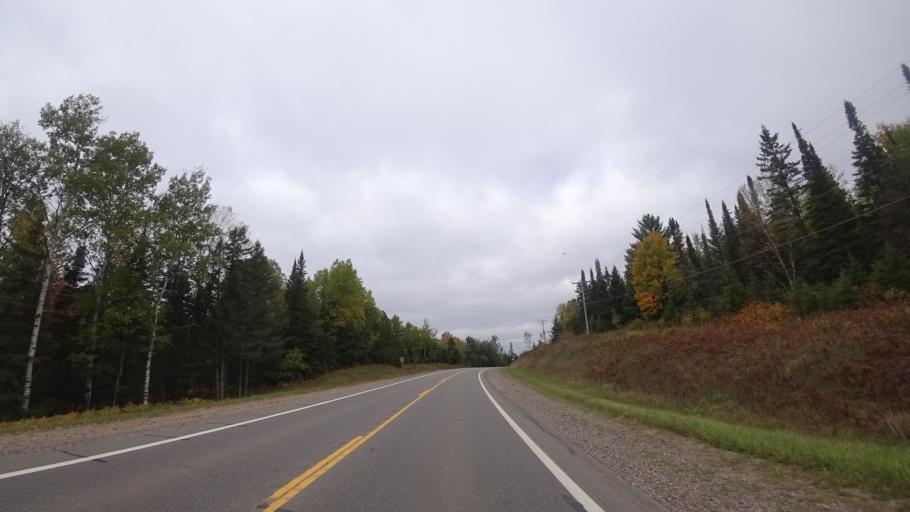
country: US
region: Michigan
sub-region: Iron County
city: Crystal Falls
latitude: 46.1155
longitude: -88.0851
